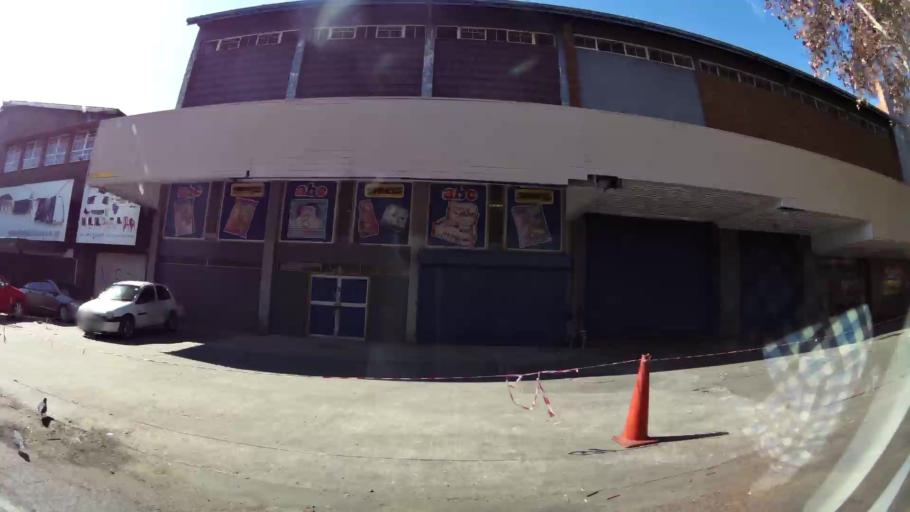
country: ZA
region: Gauteng
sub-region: City of Tshwane Metropolitan Municipality
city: Pretoria
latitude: -25.7421
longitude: 28.1975
